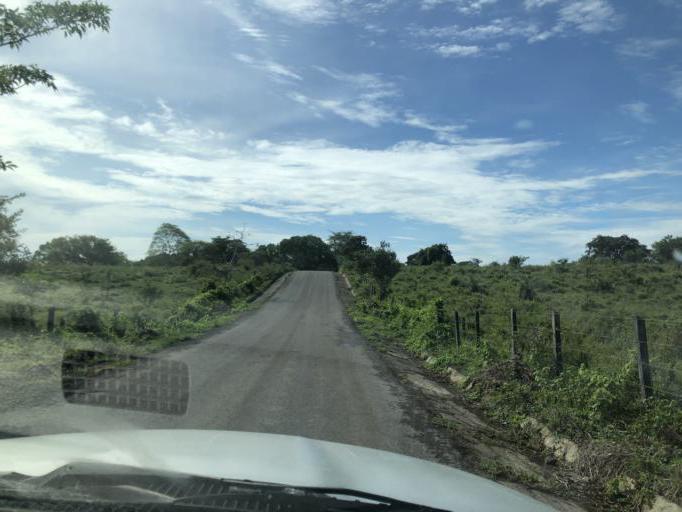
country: MX
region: Veracruz
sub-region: Alto Lucero de Gutierrez Barrios
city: Palma Sola
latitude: 19.8050
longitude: -96.5438
